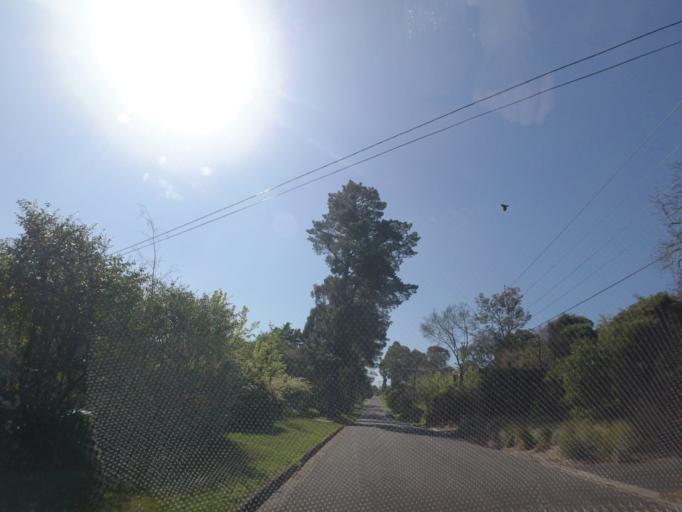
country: AU
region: Victoria
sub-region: Manningham
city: Park Orchards
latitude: -37.7847
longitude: 145.2255
